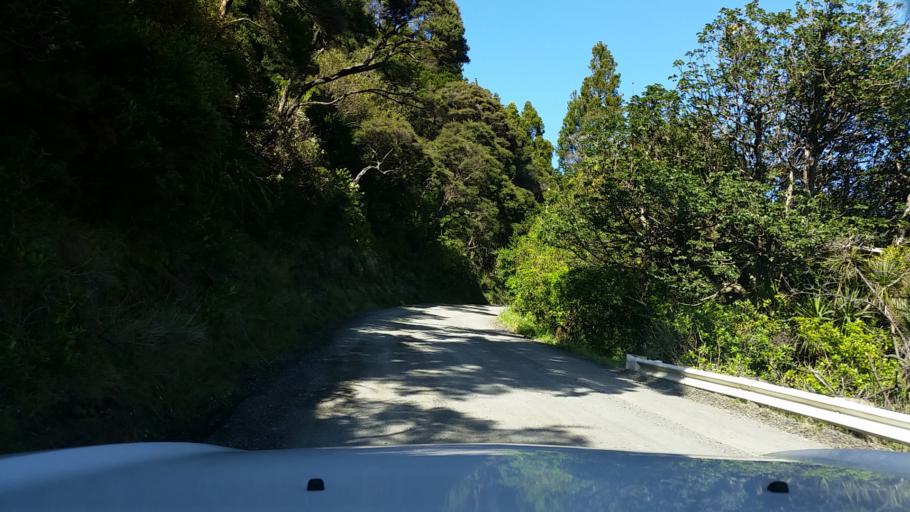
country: NZ
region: Auckland
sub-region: Auckland
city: Titirangi
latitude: -37.0205
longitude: 174.5436
